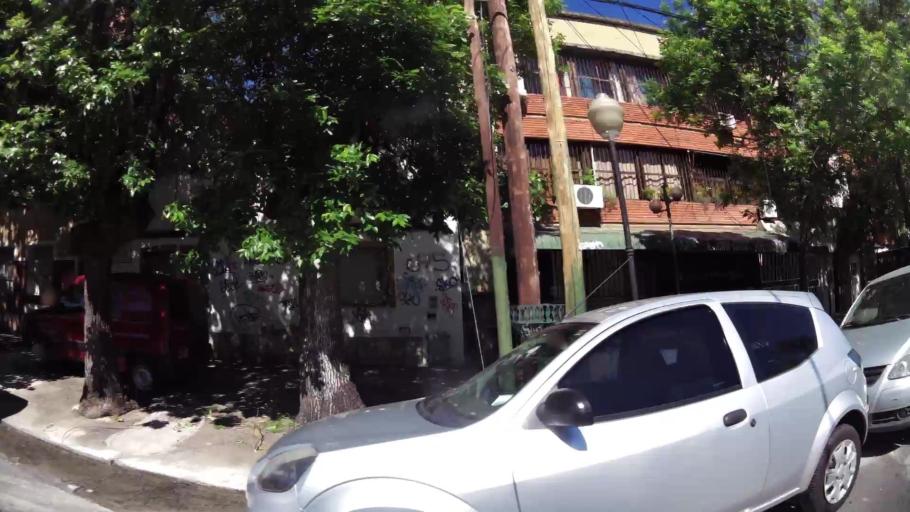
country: AR
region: Buenos Aires
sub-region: Partido de Lomas de Zamora
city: Lomas de Zamora
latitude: -34.7581
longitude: -58.4081
